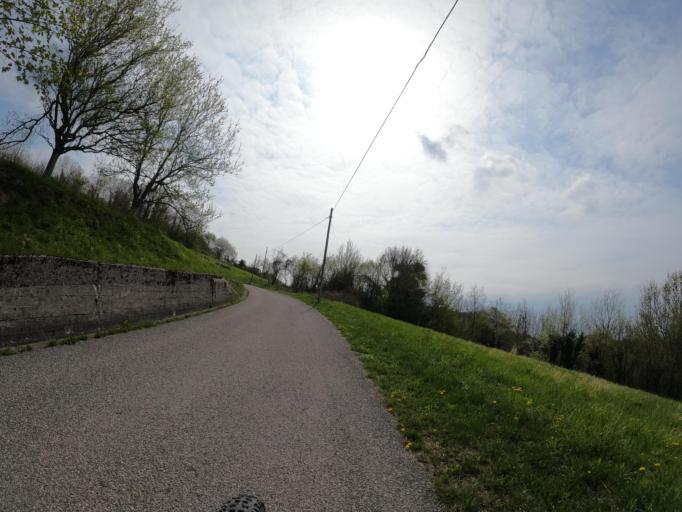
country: IT
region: Friuli Venezia Giulia
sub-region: Provincia di Udine
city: Clodig
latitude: 46.1441
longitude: 13.6129
